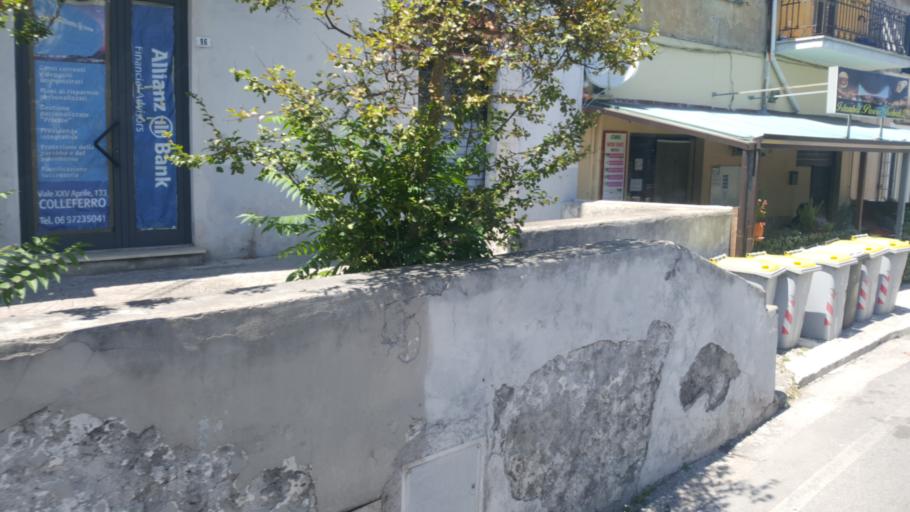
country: IT
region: Latium
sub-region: Citta metropolitana di Roma Capitale
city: Colleferro
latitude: 41.7407
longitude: 13.0012
